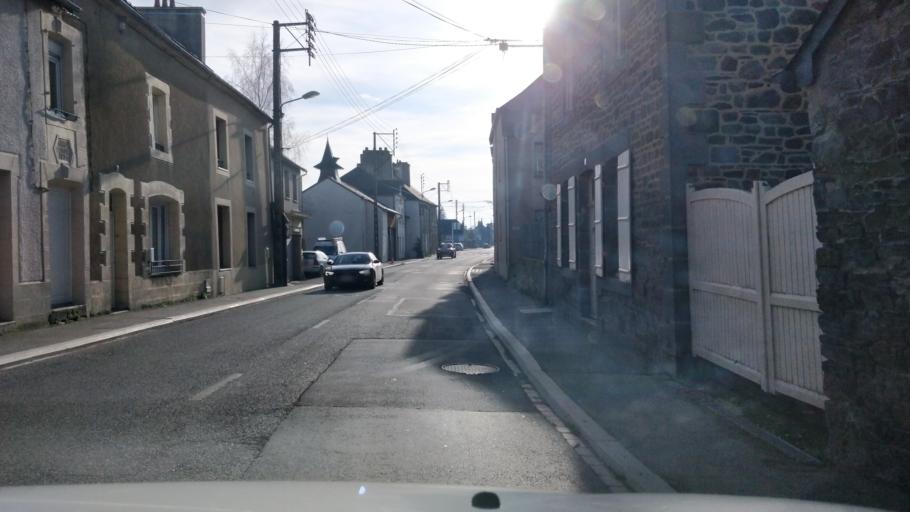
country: FR
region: Brittany
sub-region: Departement d'Ille-et-Vilaine
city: Dol-de-Bretagne
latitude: 48.5480
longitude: -1.7592
